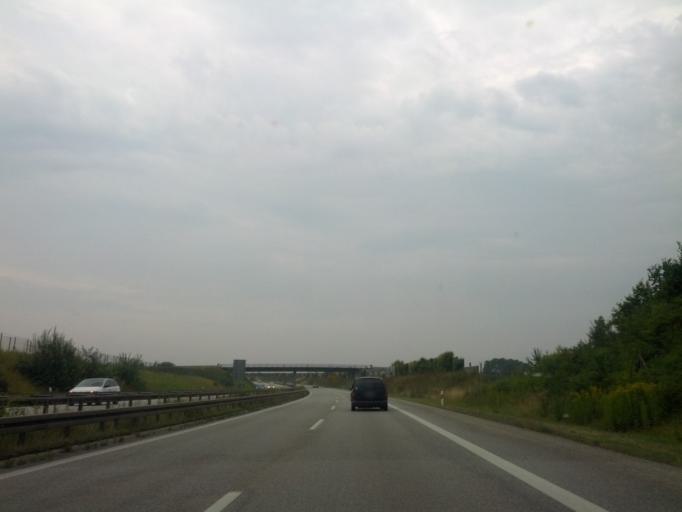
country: DE
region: Mecklenburg-Vorpommern
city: Kritzmow
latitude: 54.0817
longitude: 12.0601
